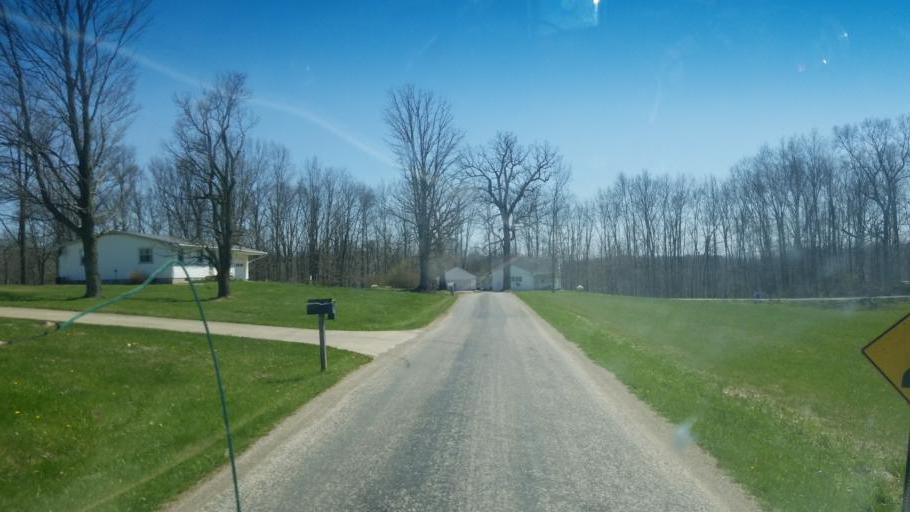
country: US
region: Ohio
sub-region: Ashland County
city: Ashland
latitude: 40.8374
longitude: -82.3865
